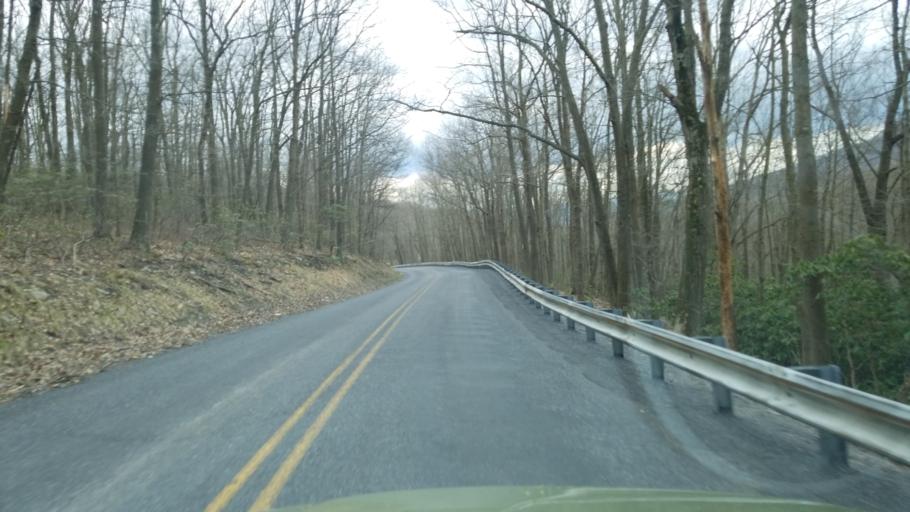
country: US
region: Pennsylvania
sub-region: Blair County
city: Tipton
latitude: 40.7028
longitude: -78.3382
